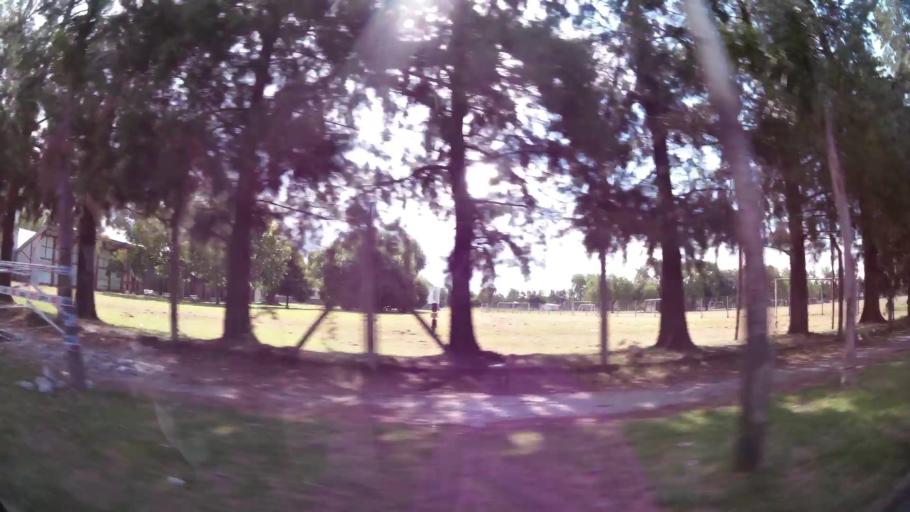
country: AR
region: Buenos Aires
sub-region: Partido de Tigre
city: Tigre
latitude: -34.4690
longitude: -58.5763
